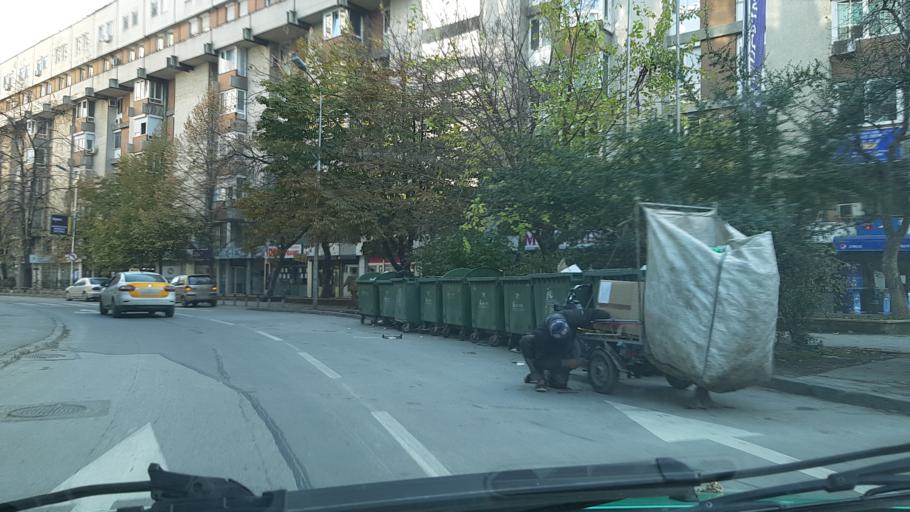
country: MK
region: Karpos
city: Skopje
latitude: 41.9933
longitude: 21.4281
